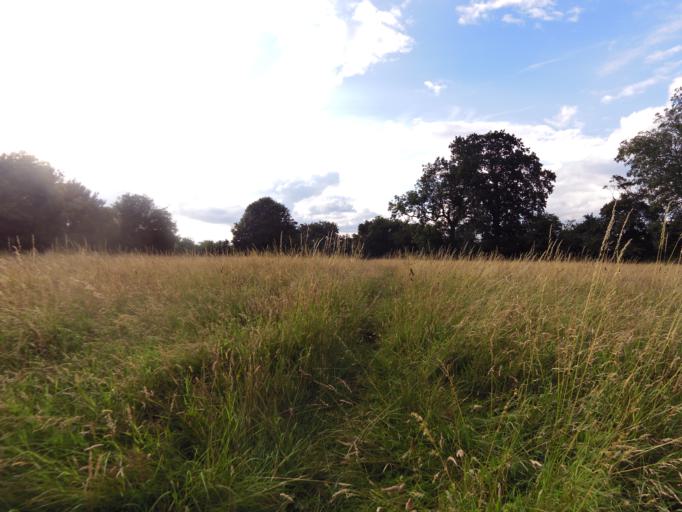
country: GB
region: England
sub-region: Suffolk
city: Ipswich
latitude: 52.0841
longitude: 1.1643
